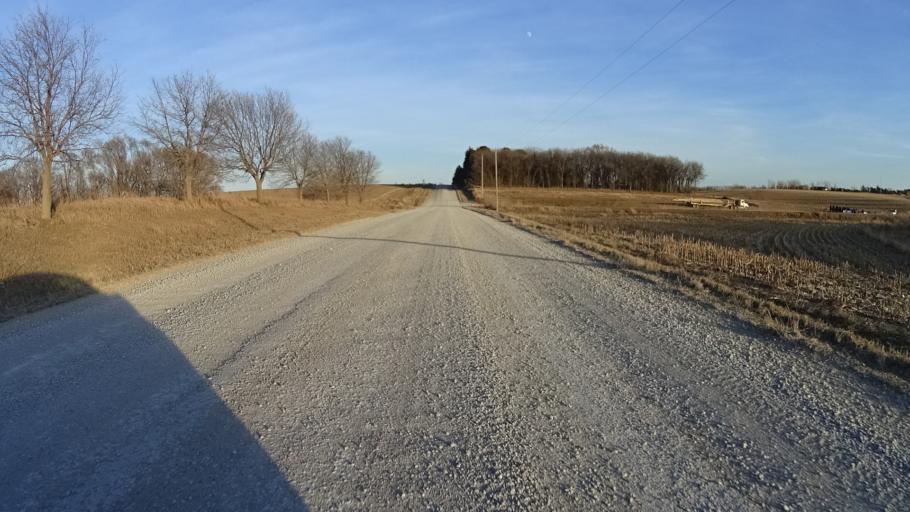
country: US
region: Nebraska
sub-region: Sarpy County
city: Springfield
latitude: 41.1326
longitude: -96.1172
